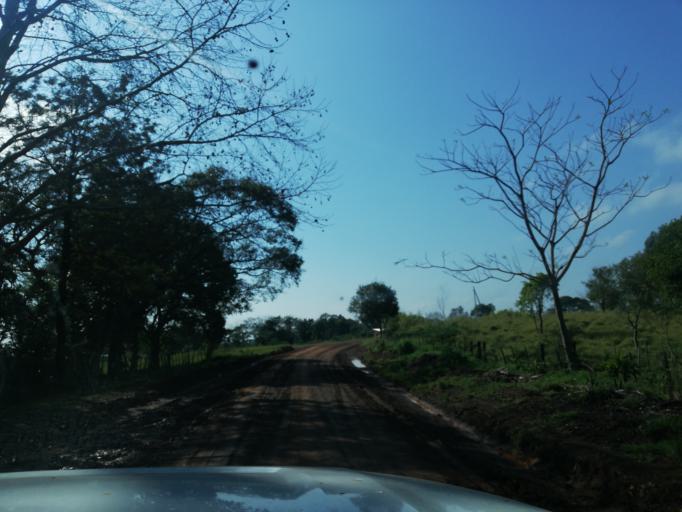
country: AR
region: Misiones
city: Cerro Azul
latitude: -27.6306
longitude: -55.5099
